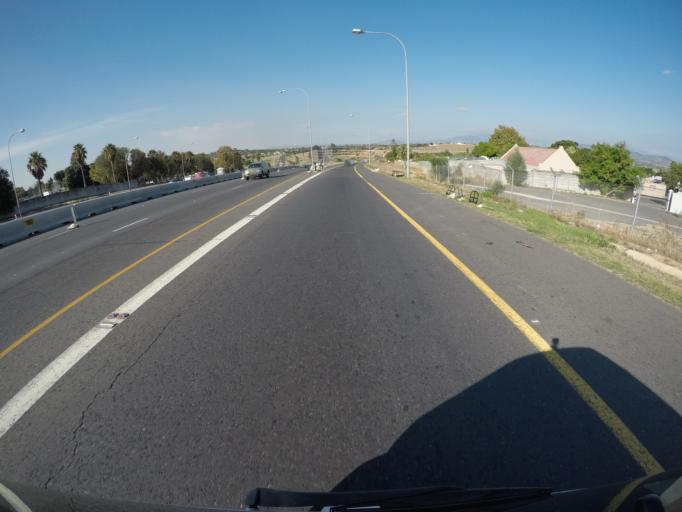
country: ZA
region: Western Cape
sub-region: City of Cape Town
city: Kraaifontein
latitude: -33.8751
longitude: 18.6636
